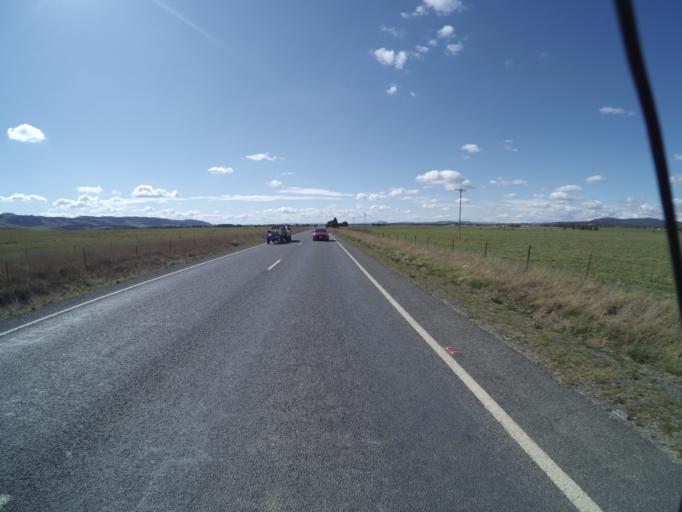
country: AU
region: New South Wales
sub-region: Palerang
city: Bungendore
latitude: -35.2846
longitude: 149.4216
